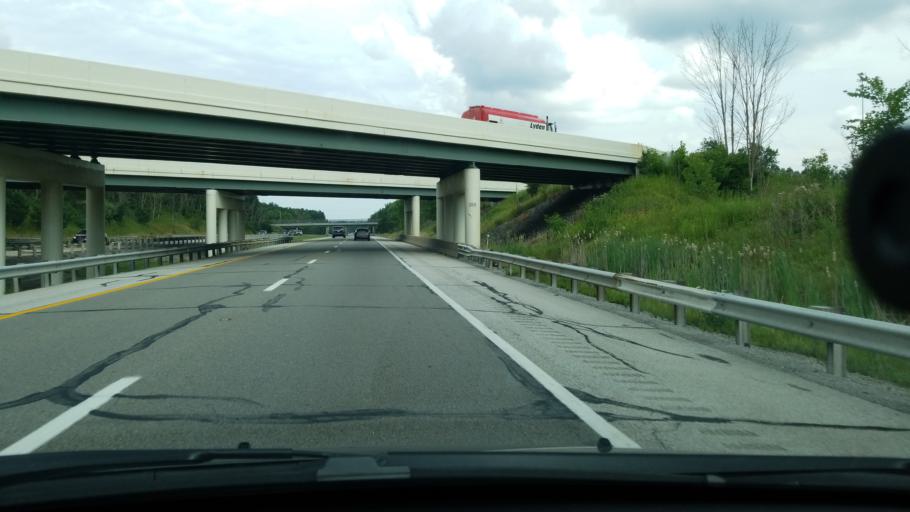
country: US
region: Ohio
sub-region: Mahoning County
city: Canfield
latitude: 41.0333
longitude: -80.7412
